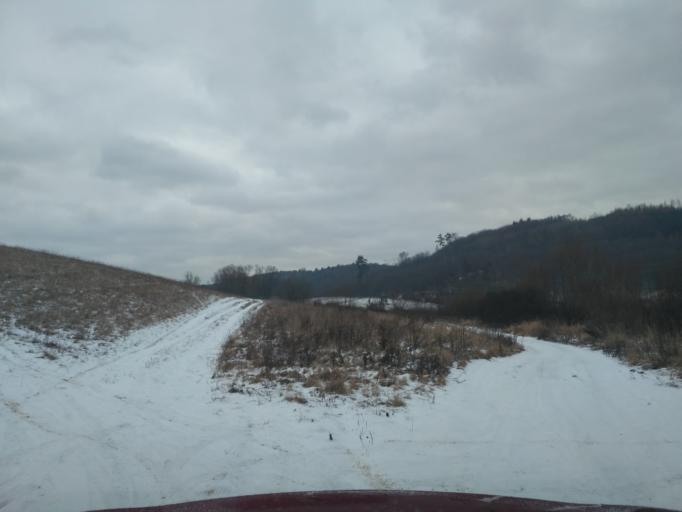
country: SK
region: Presovsky
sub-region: Okres Presov
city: Presov
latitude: 49.0022
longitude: 21.1760
